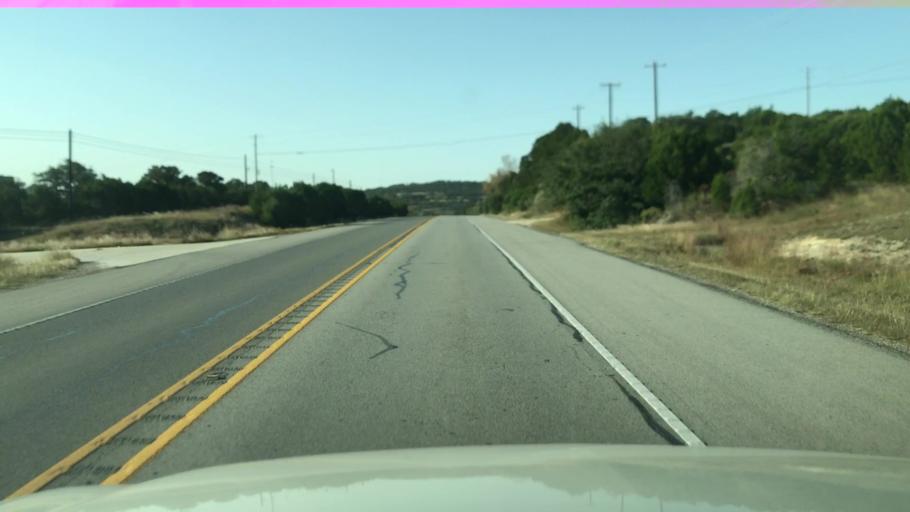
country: US
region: Texas
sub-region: Blanco County
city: Johnson City
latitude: 30.1914
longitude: -98.3771
